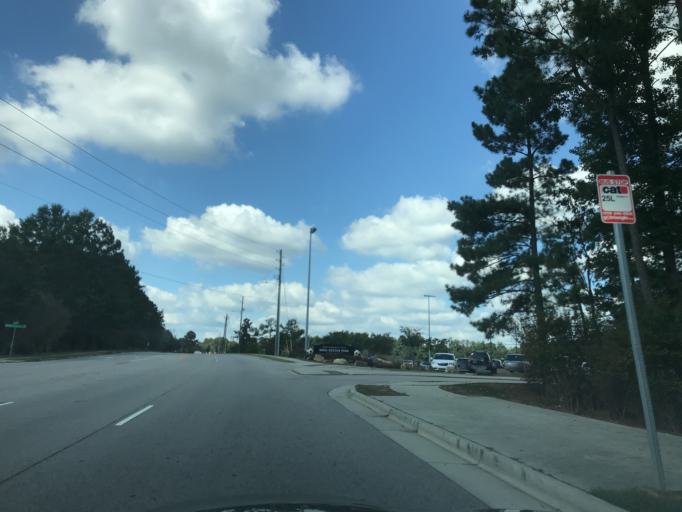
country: US
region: North Carolina
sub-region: Wake County
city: Rolesville
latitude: 35.8821
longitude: -78.5496
